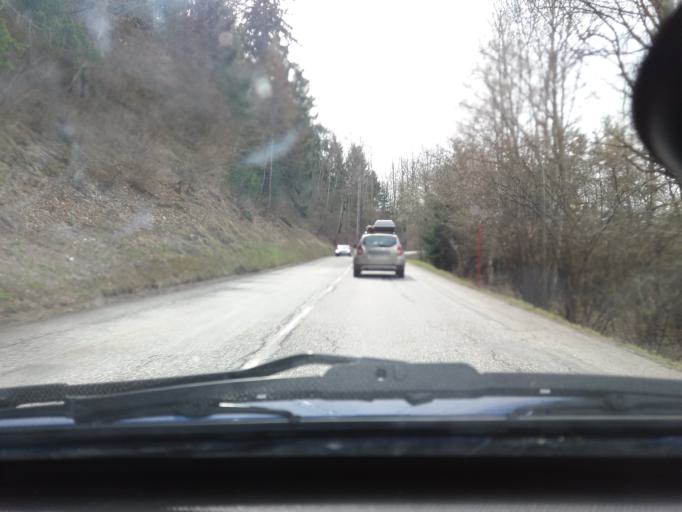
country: FR
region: Rhone-Alpes
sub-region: Departement de la Savoie
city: Macot-la-Plagne
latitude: 45.5459
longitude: 6.6717
